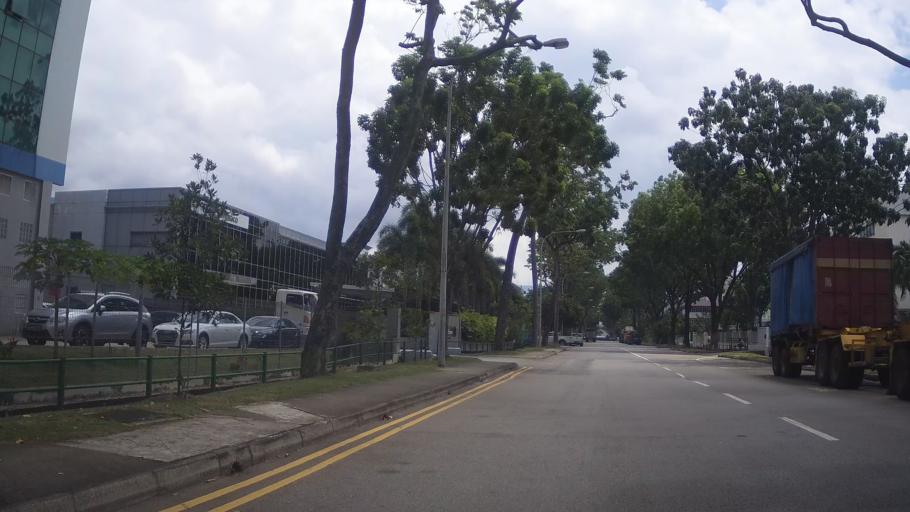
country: MY
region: Johor
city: Johor Bahru
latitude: 1.3174
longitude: 103.6717
